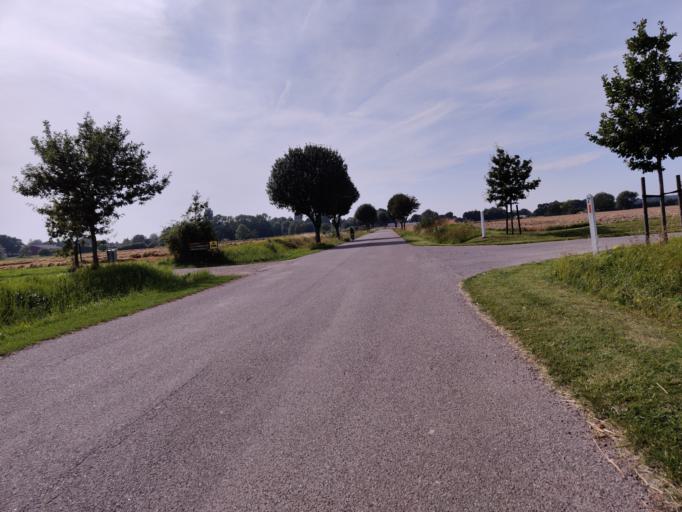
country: DK
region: Zealand
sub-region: Guldborgsund Kommune
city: Nykobing Falster
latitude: 54.6350
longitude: 11.9120
